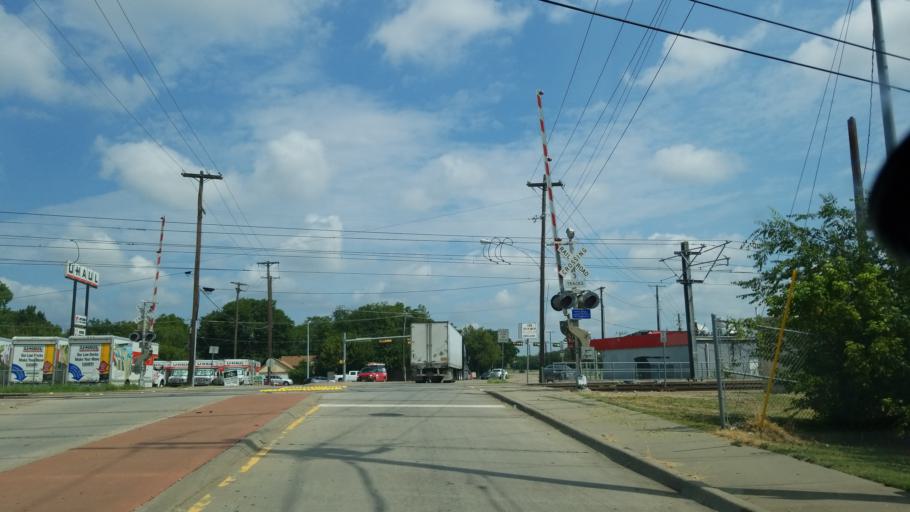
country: US
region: Texas
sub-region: Dallas County
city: Garland
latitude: 32.9152
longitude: -96.6401
